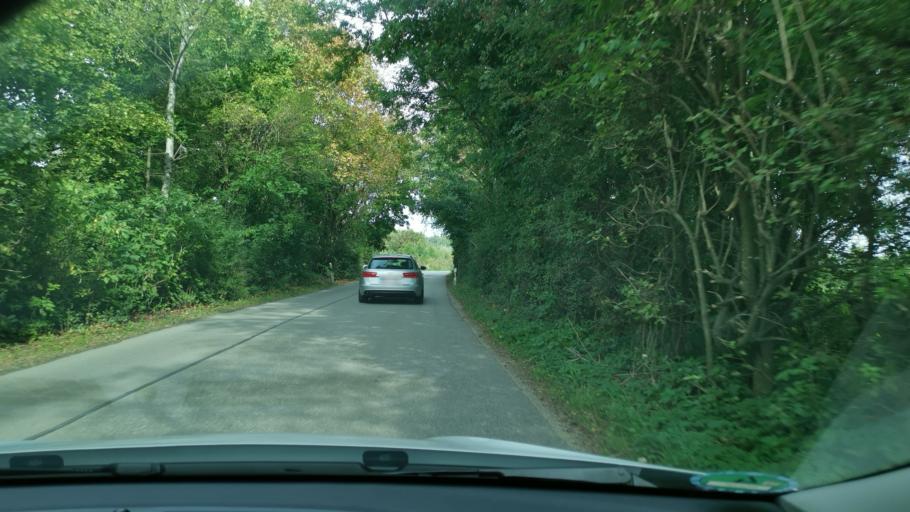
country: DE
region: Bavaria
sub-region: Upper Bavaria
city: Bergkirchen
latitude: 48.2465
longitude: 11.3593
